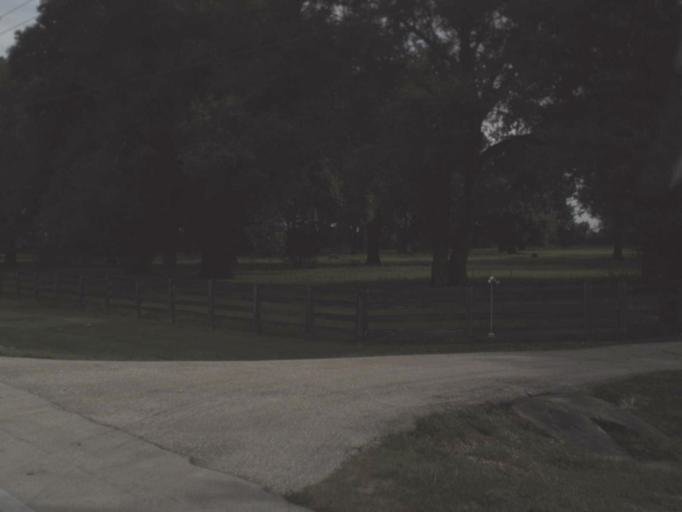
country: US
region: Florida
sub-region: DeSoto County
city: Southeast Arcadia
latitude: 27.1856
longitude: -81.8280
